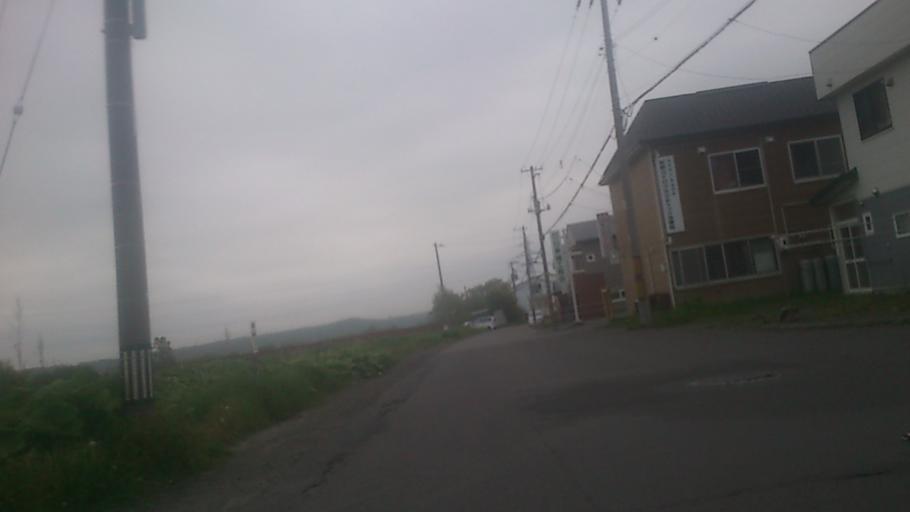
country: JP
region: Hokkaido
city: Kushiro
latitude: 42.9989
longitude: 144.4179
